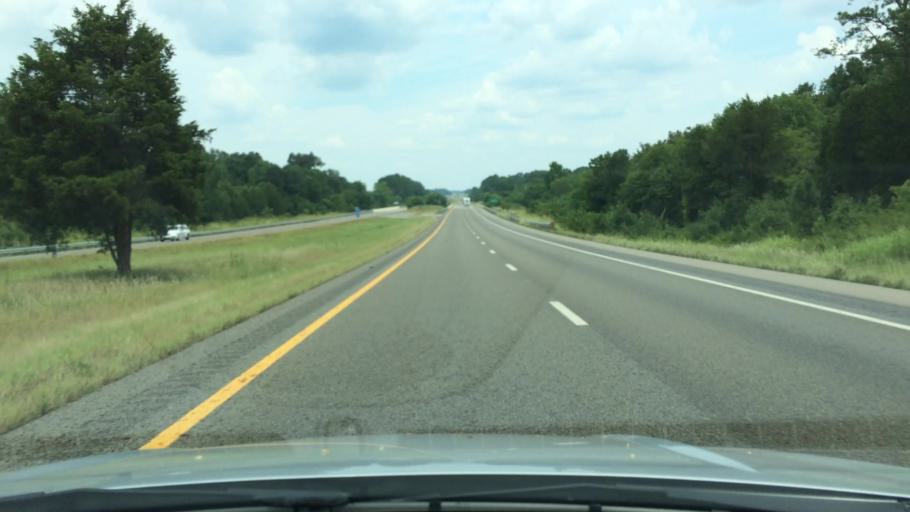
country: US
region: Tennessee
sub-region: Maury County
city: Columbia
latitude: 35.5619
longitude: -86.9065
